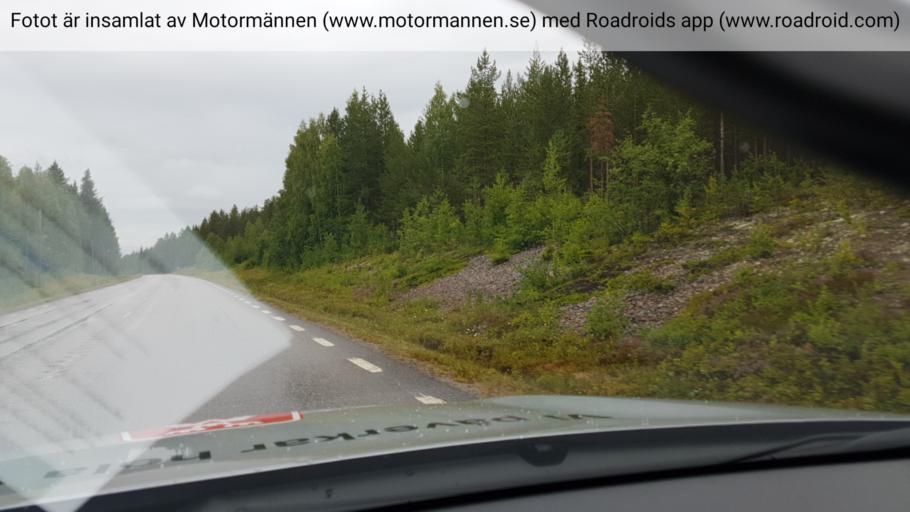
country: SE
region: Norrbotten
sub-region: Alvsbyns Kommun
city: AElvsbyn
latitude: 66.1202
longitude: 20.9223
